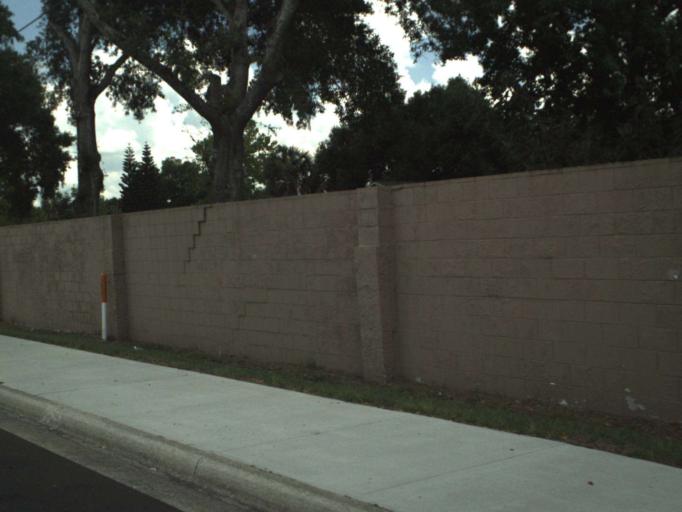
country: US
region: Florida
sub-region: Seminole County
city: Longwood
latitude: 28.6979
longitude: -81.3701
